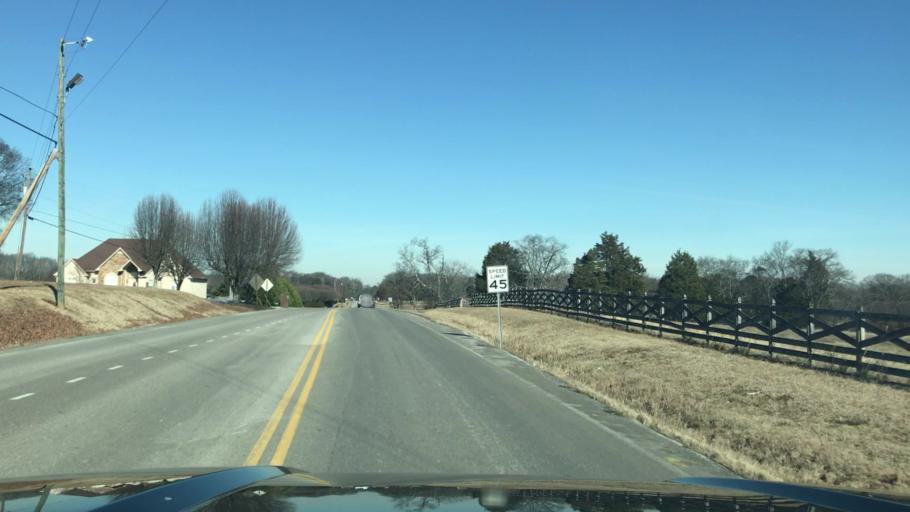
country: US
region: Tennessee
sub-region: Wilson County
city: Lebanon
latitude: 36.1948
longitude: -86.3415
